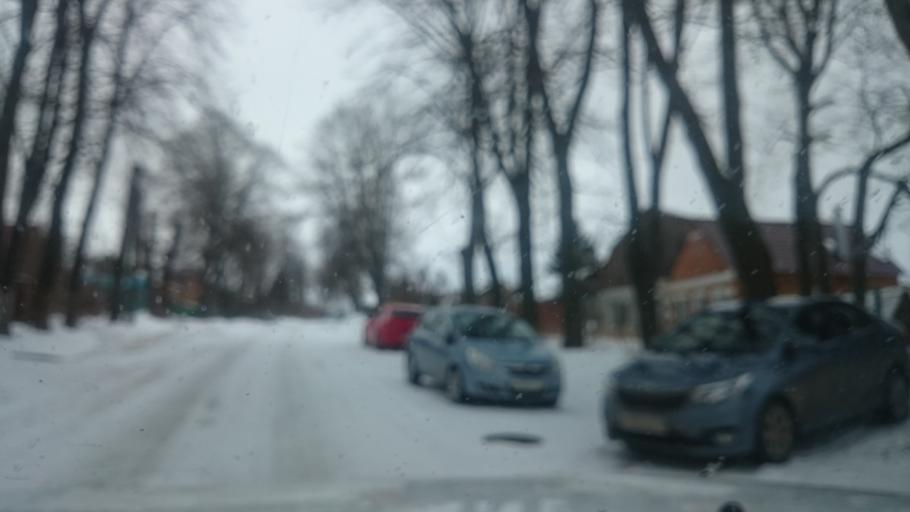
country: RU
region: Tula
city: Pervomayskiy
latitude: 54.0724
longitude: 37.5292
